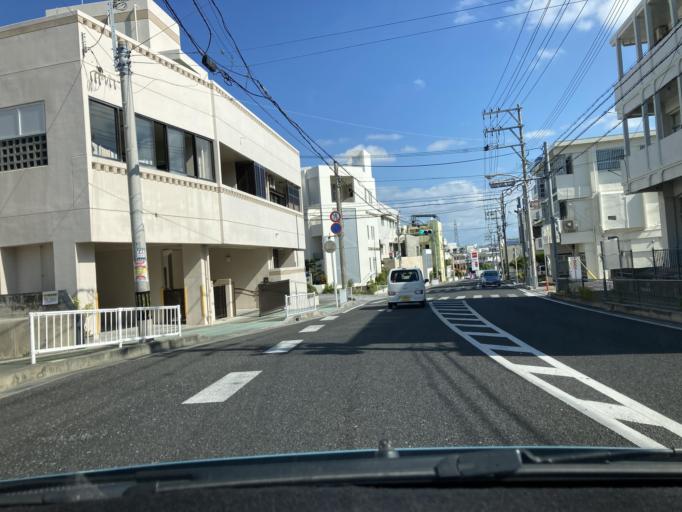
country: JP
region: Okinawa
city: Tomigusuku
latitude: 26.1900
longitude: 127.6691
